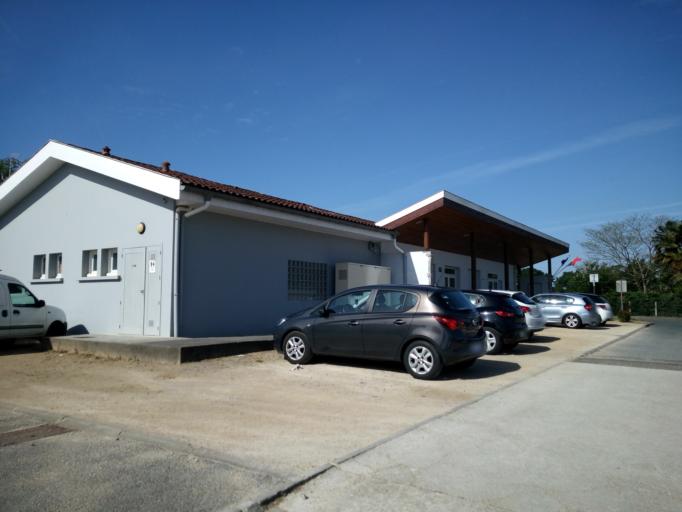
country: FR
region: Aquitaine
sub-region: Departement des Landes
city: Saint-Martin-de-Hinx
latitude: 43.5609
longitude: -1.2719
